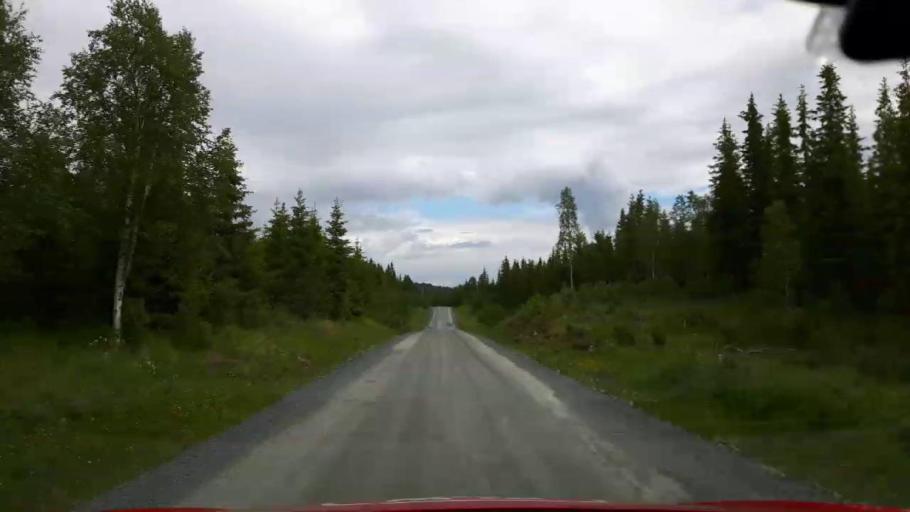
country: NO
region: Nord-Trondelag
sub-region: Lierne
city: Sandvika
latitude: 64.1445
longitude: 13.9240
